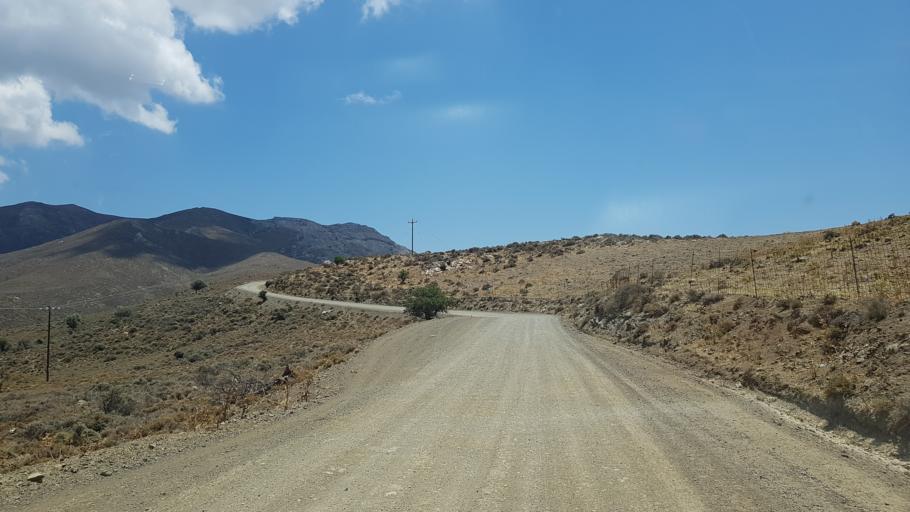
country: GR
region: Crete
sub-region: Nomos Irakleiou
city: Agioi Deka
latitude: 34.9716
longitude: 24.9808
